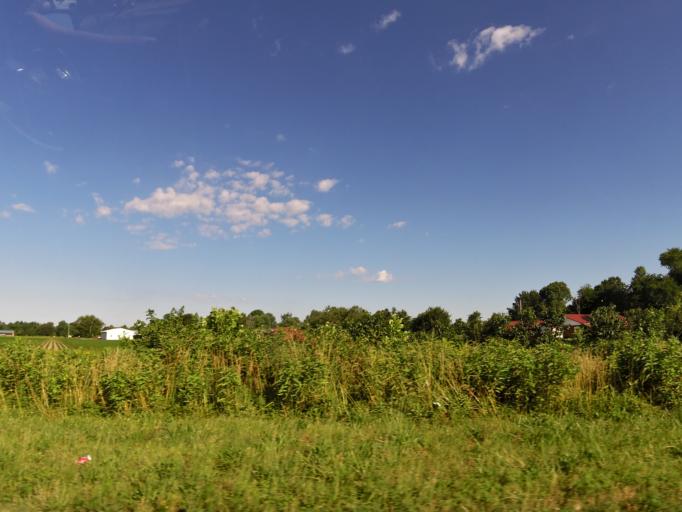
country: US
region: Arkansas
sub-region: Clay County
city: Corning
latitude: 36.5311
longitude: -90.5357
